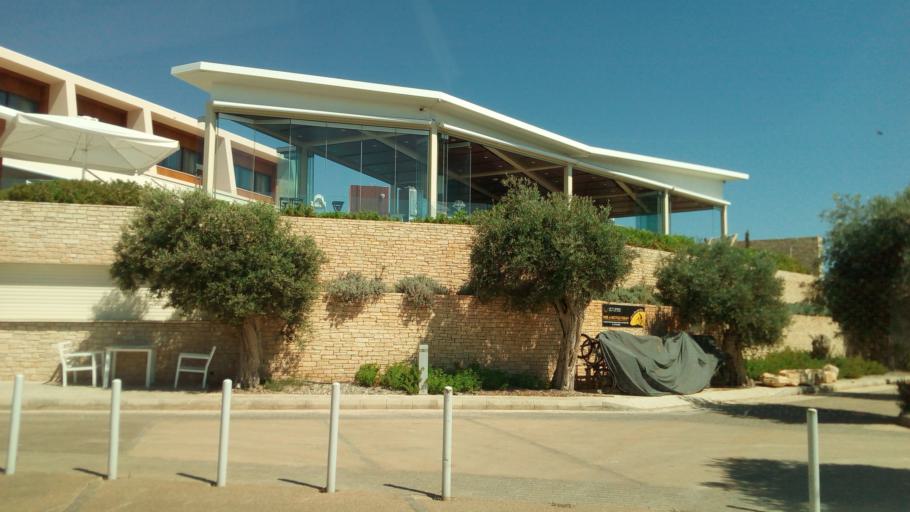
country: CY
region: Pafos
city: Pegeia
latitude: 34.8947
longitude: 32.3235
